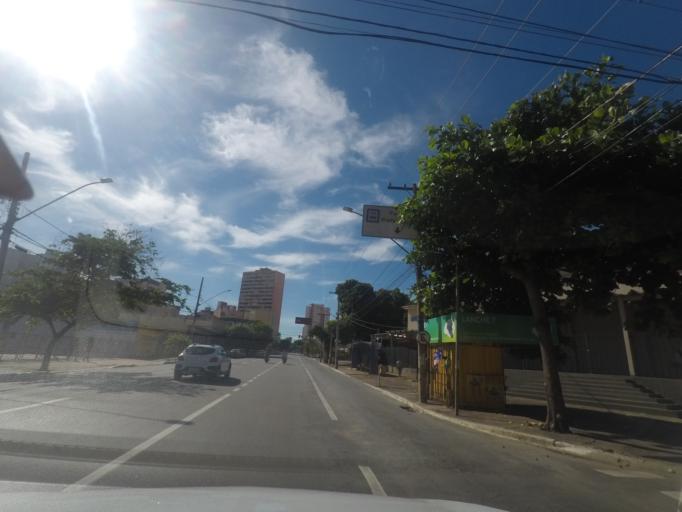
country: BR
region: Goias
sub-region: Goiania
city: Goiania
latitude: -16.6744
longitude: -49.2632
